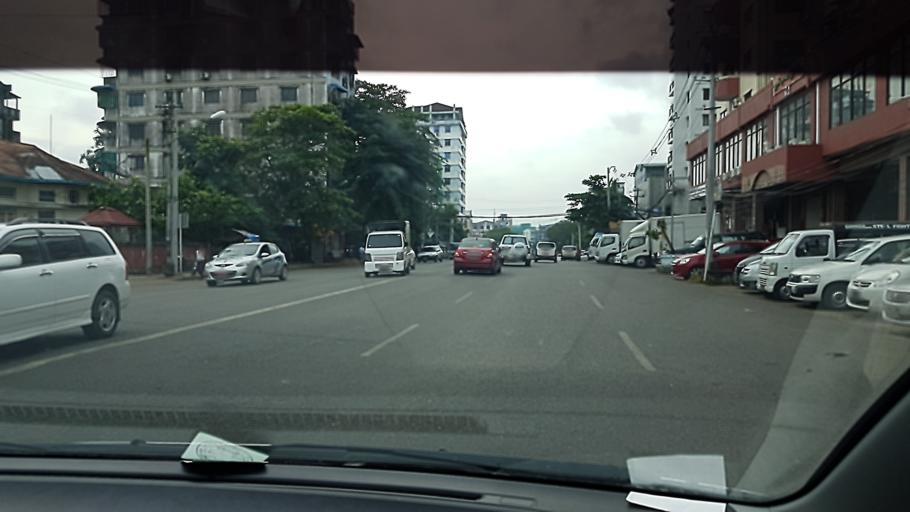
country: MM
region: Yangon
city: Yangon
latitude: 16.7987
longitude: 96.1262
